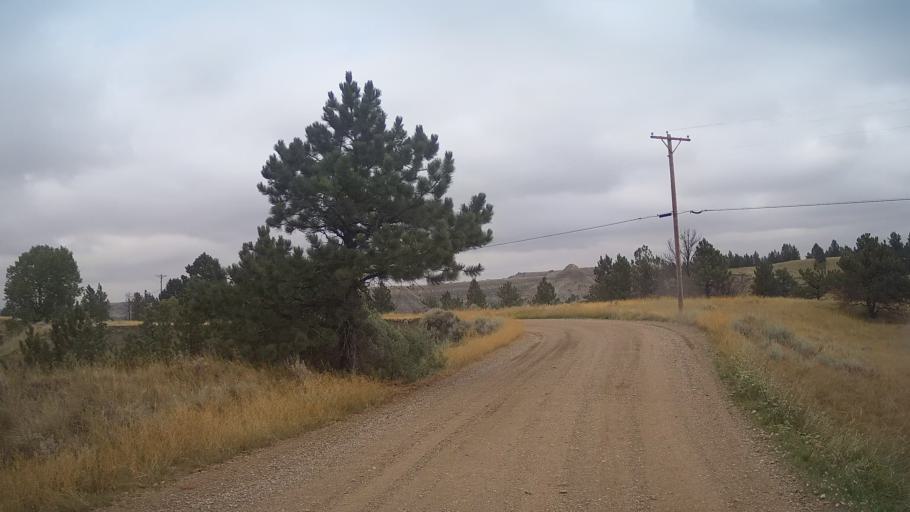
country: US
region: Montana
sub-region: Dawson County
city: Glendive
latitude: 47.0594
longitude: -104.6811
